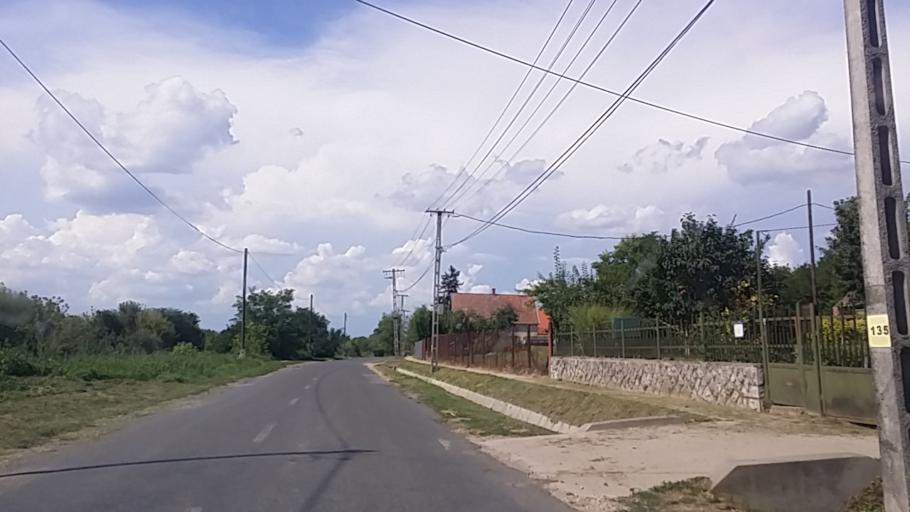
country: HU
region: Tolna
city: Hogyesz
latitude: 46.5287
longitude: 18.4454
